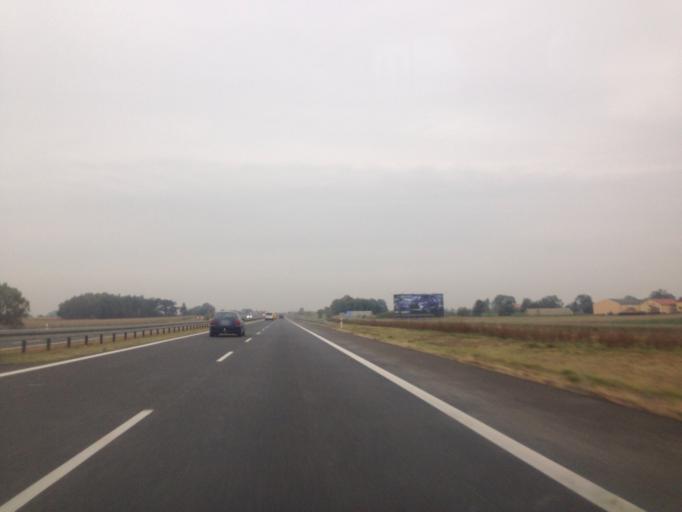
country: PL
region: Greater Poland Voivodeship
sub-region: Powiat poznanski
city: Kleszczewo
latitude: 52.3511
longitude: 17.1810
